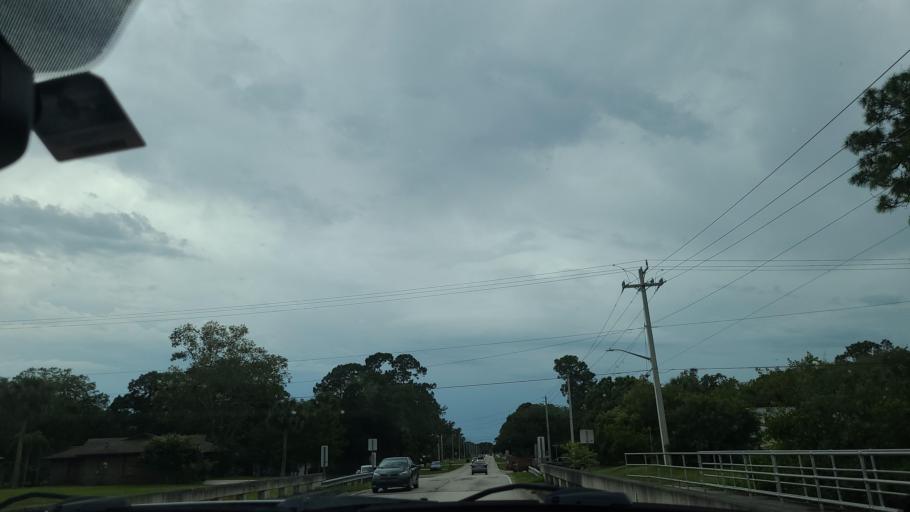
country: US
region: Florida
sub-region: Brevard County
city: West Melbourne
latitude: 28.0133
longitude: -80.6456
